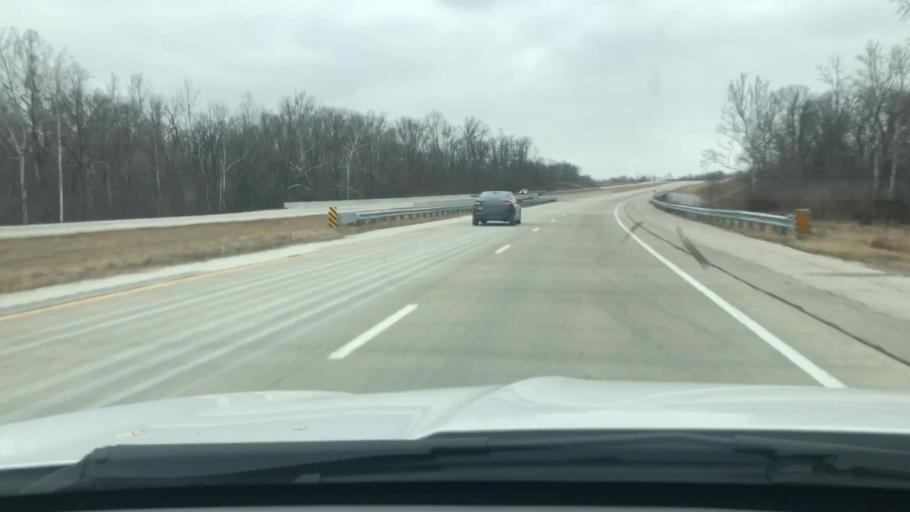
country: US
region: Indiana
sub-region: Carroll County
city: Delphi
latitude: 40.5118
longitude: -86.7226
